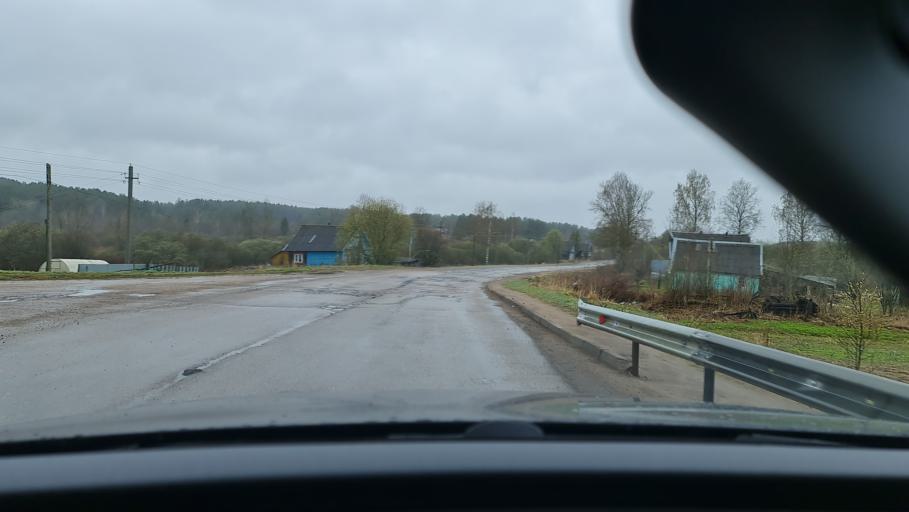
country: RU
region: Novgorod
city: Valday
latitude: 58.0356
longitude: 32.9483
